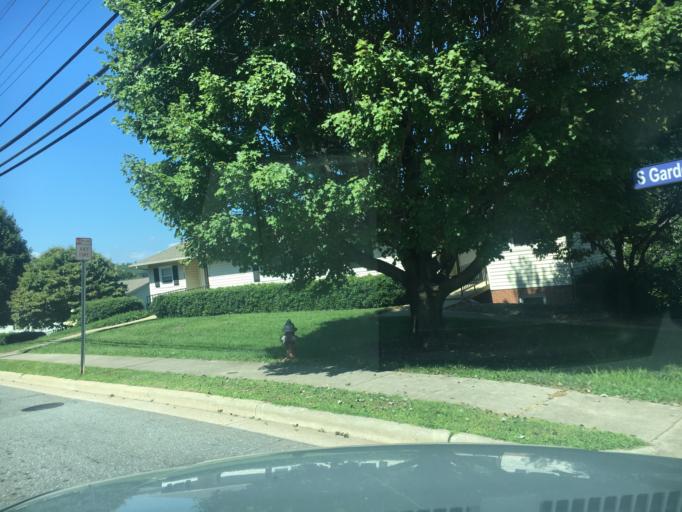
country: US
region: North Carolina
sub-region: McDowell County
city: Marion
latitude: 35.6808
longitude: -82.0057
